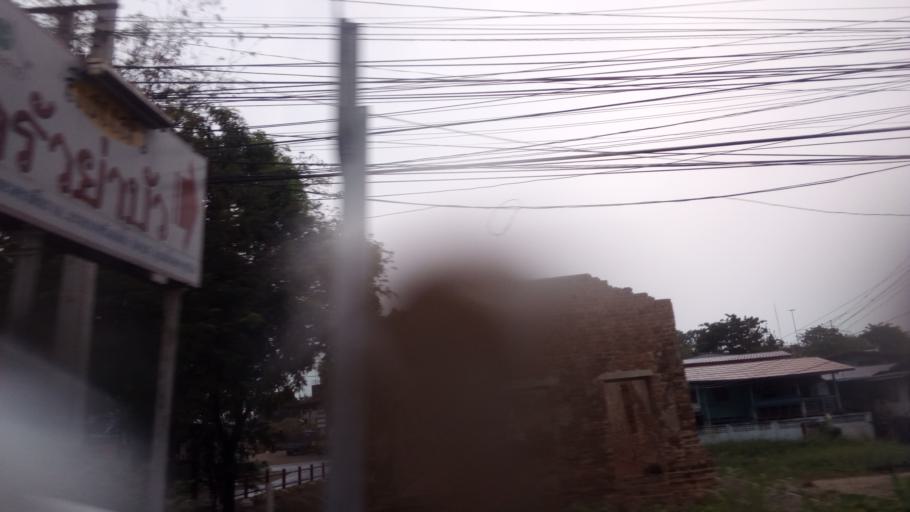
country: TH
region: Phra Nakhon Si Ayutthaya
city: Phra Nakhon Si Ayutthaya
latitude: 14.3462
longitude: 100.5848
